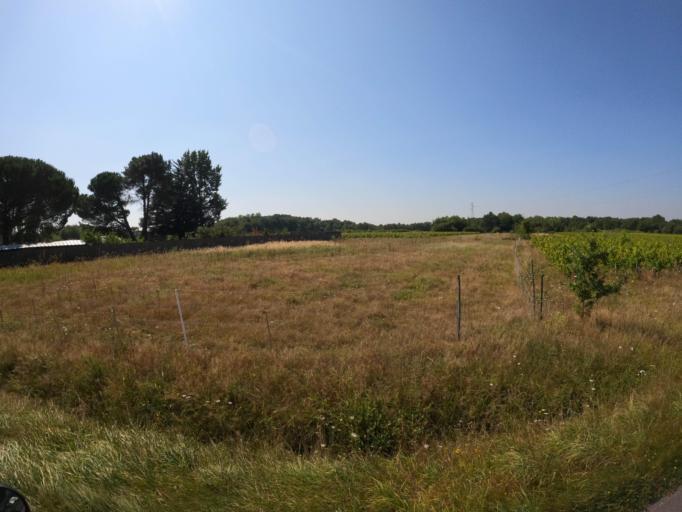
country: FR
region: Pays de la Loire
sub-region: Departement de la Loire-Atlantique
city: Pont-Saint-Martin
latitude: 47.1185
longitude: -1.5598
